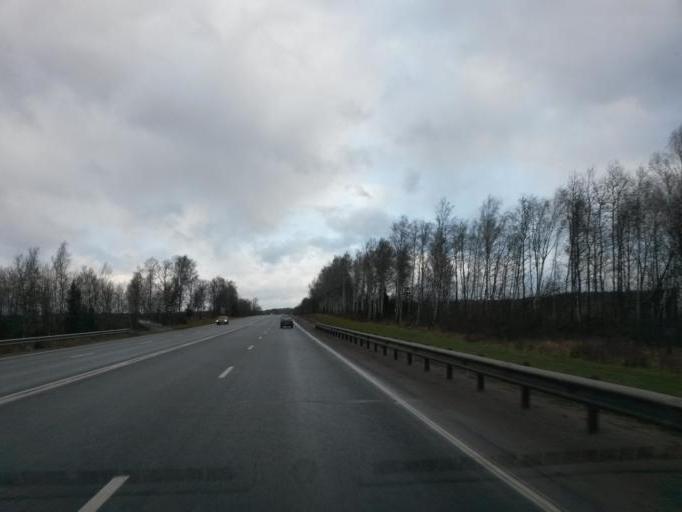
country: RU
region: Jaroslavl
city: Petrovsk
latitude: 57.0343
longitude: 39.2849
